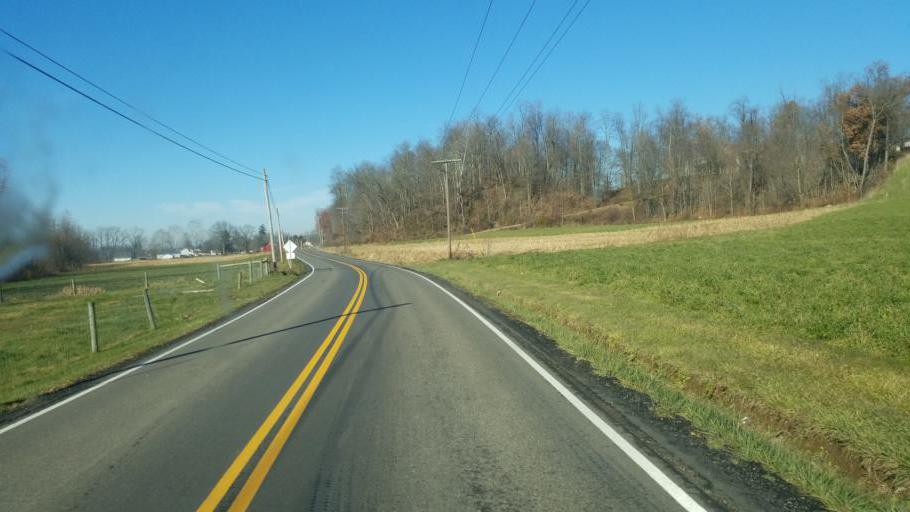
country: US
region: Ohio
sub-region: Holmes County
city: Millersburg
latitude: 40.6115
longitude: -81.8612
